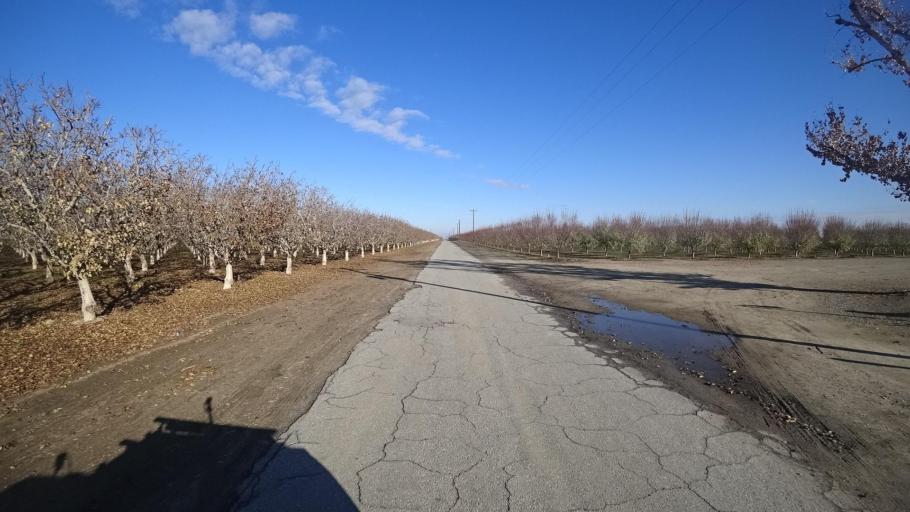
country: US
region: California
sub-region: Kern County
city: McFarland
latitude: 35.6903
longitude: -119.2942
